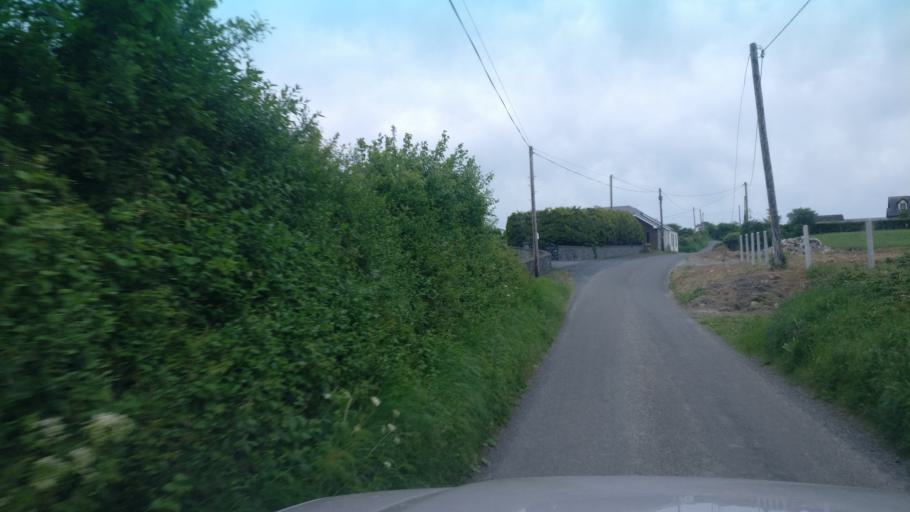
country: IE
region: Connaught
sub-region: County Galway
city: Portumna
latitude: 53.1384
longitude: -8.2908
